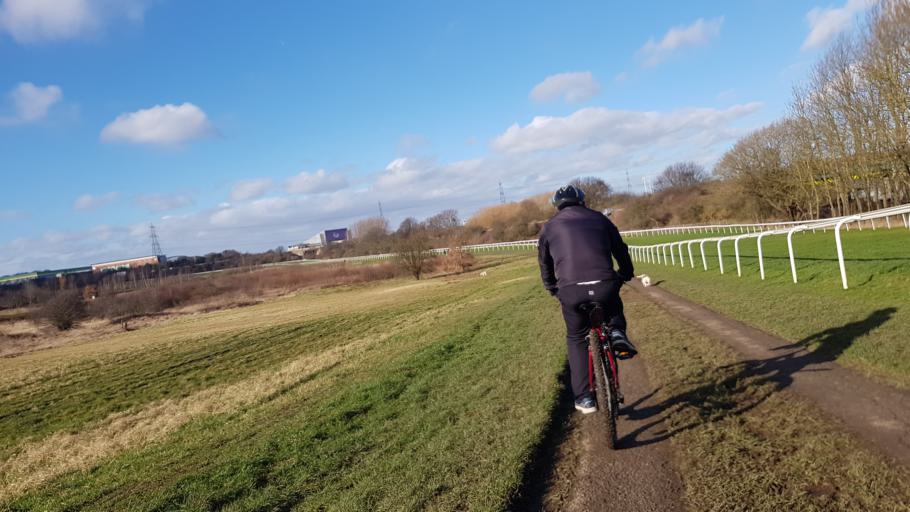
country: GB
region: England
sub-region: City and Borough of Wakefield
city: Pontefract
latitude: 53.7033
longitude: -1.3282
